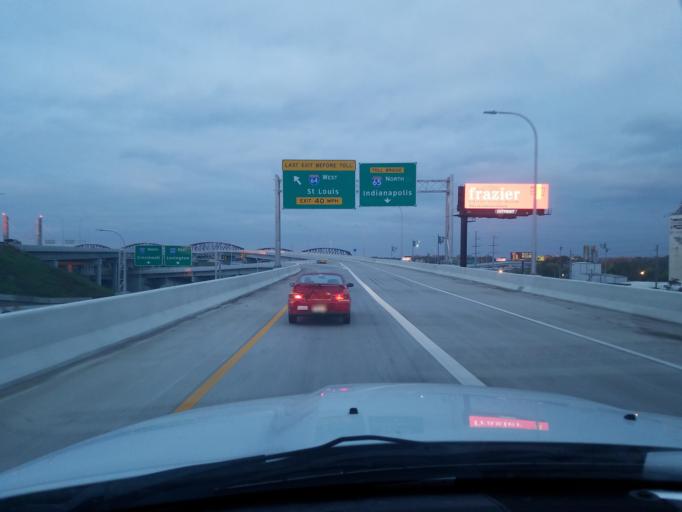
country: US
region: Kentucky
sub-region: Jefferson County
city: Louisville
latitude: 38.2562
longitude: -85.7414
